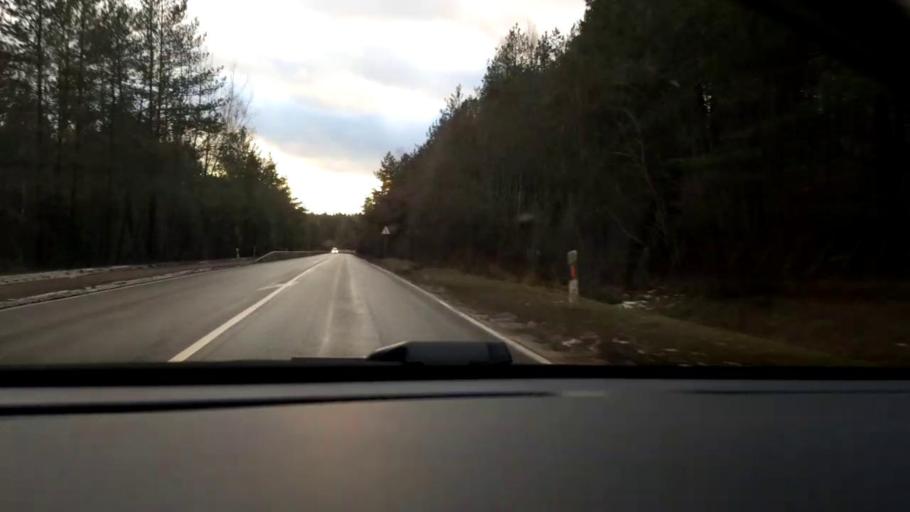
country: LT
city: Nemencine
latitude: 54.7911
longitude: 25.3878
